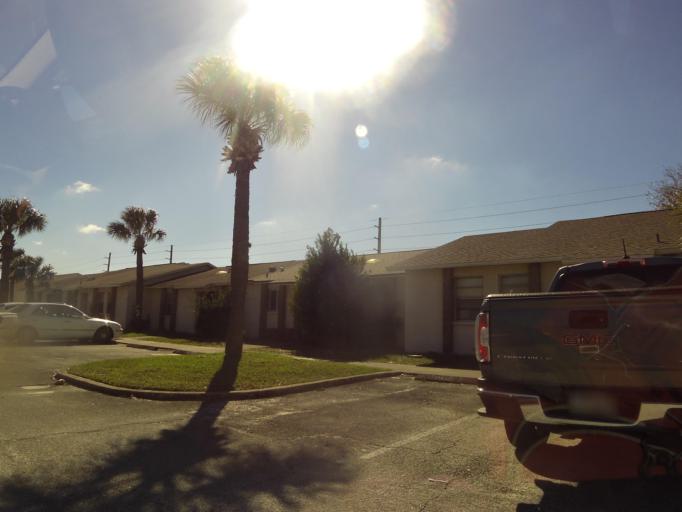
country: US
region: Florida
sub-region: Brevard County
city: Cocoa
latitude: 28.3833
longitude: -80.7545
